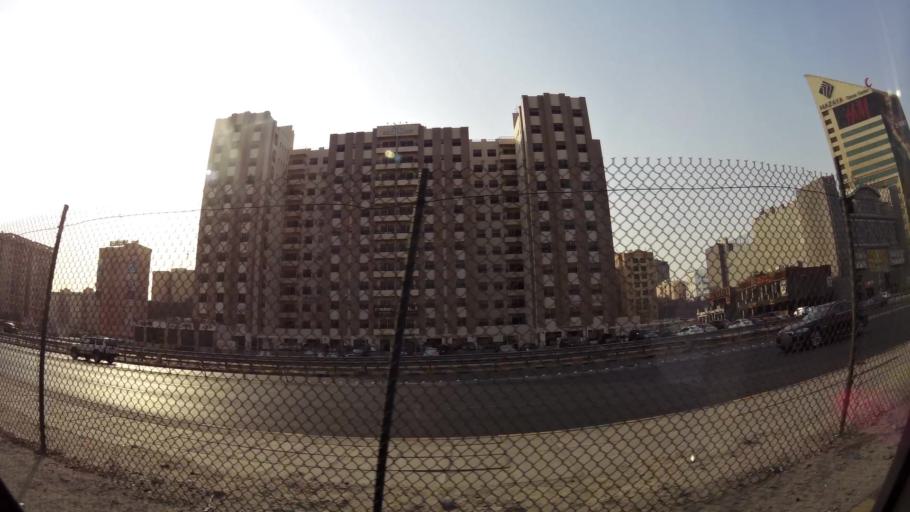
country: KW
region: Muhafazat Hawalli
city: Hawalli
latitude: 29.3240
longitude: 48.0164
